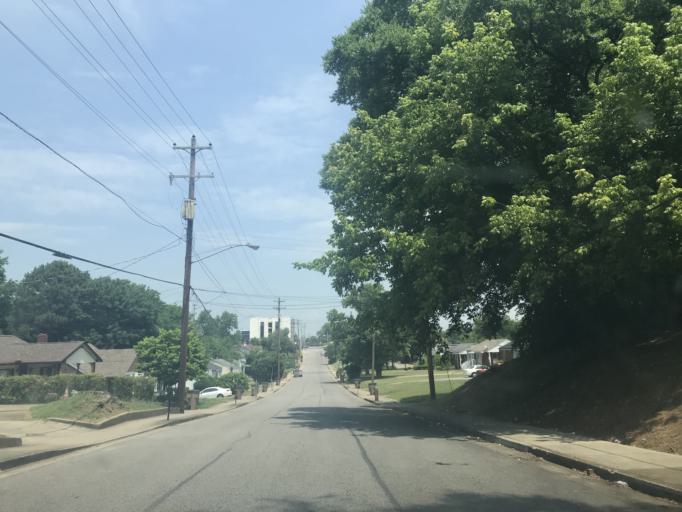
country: US
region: Tennessee
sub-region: Davidson County
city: Nashville
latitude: 36.1830
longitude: -86.8192
